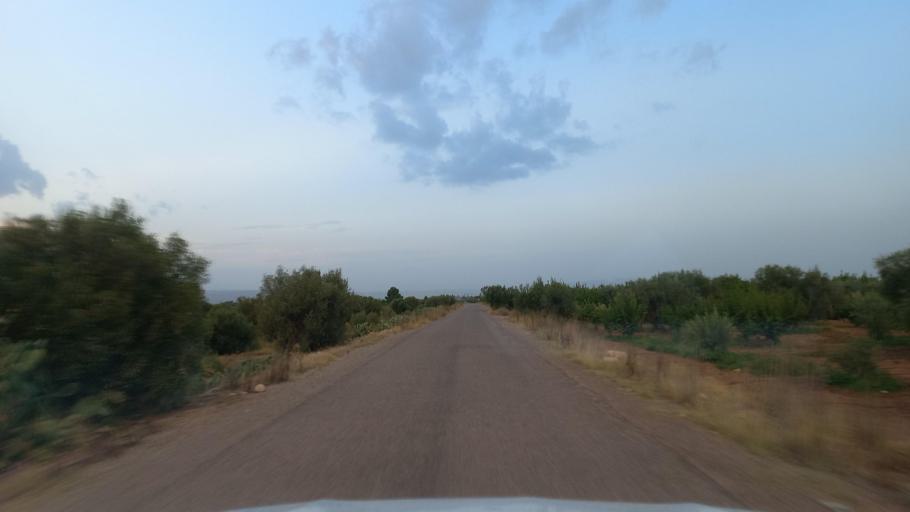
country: TN
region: Al Qasrayn
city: Kasserine
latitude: 35.2648
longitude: 9.0501
